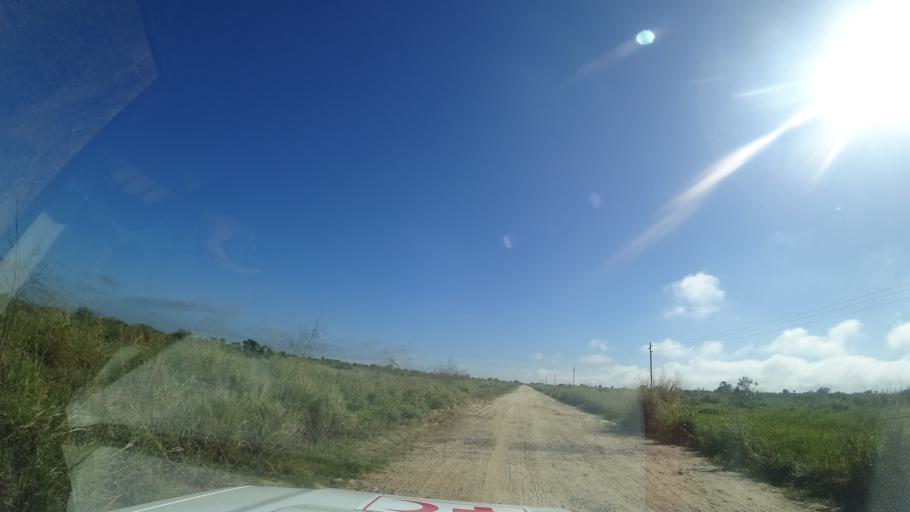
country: MZ
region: Sofala
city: Dondo
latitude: -19.4497
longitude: 34.5624
